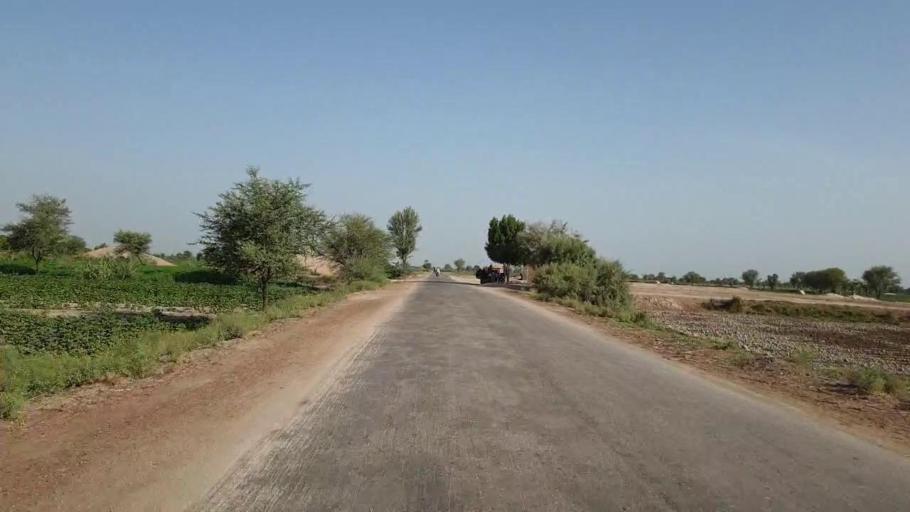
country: PK
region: Sindh
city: Nawabshah
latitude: 26.1352
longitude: 68.4542
